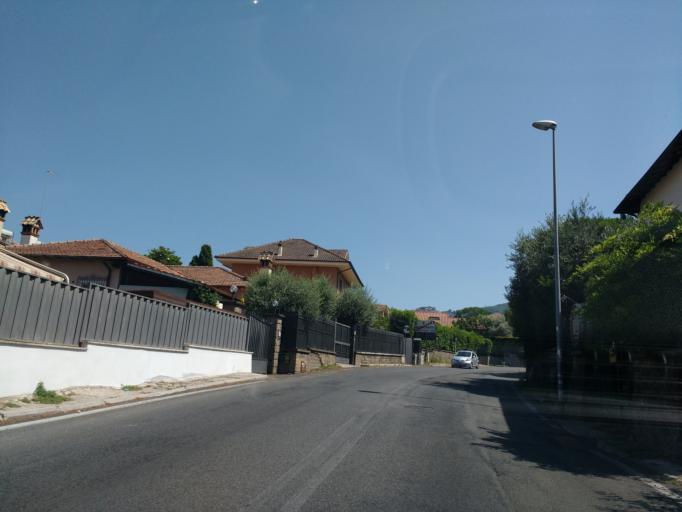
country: IT
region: Latium
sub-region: Citta metropolitana di Roma Capitale
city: Grottaferrata
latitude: 41.7797
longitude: 12.6852
